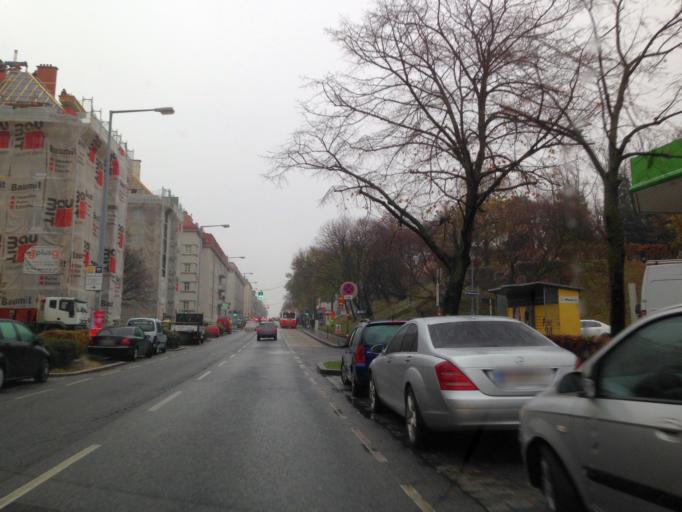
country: AT
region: Vienna
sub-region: Wien Stadt
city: Vienna
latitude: 48.2071
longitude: 16.3136
